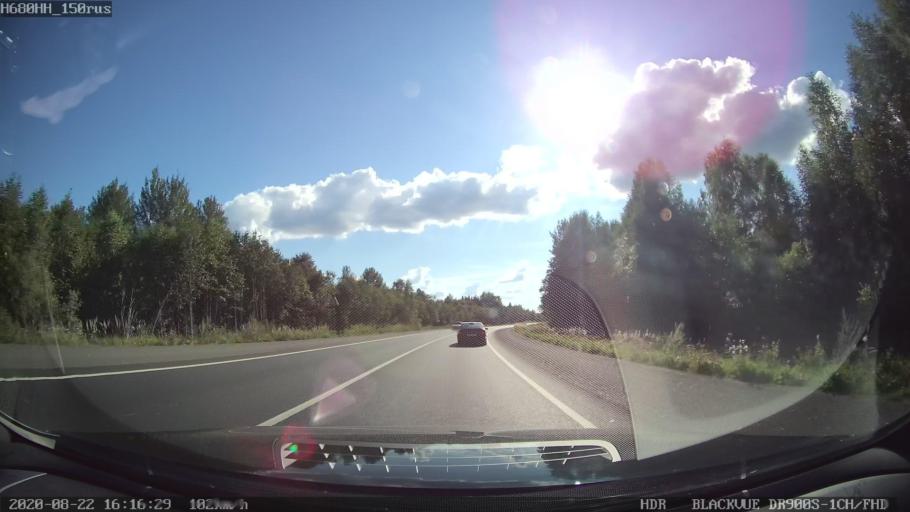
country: RU
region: Tverskaya
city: Rameshki
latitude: 57.4335
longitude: 36.1787
